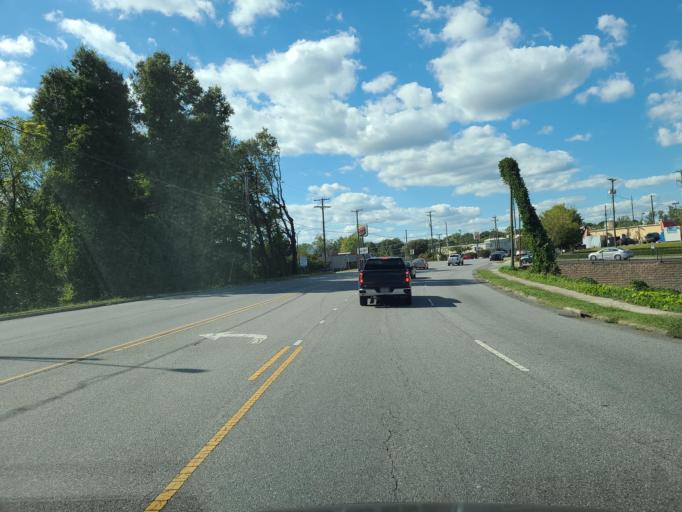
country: US
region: North Carolina
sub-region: Gaston County
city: Gastonia
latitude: 35.2586
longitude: -81.2147
